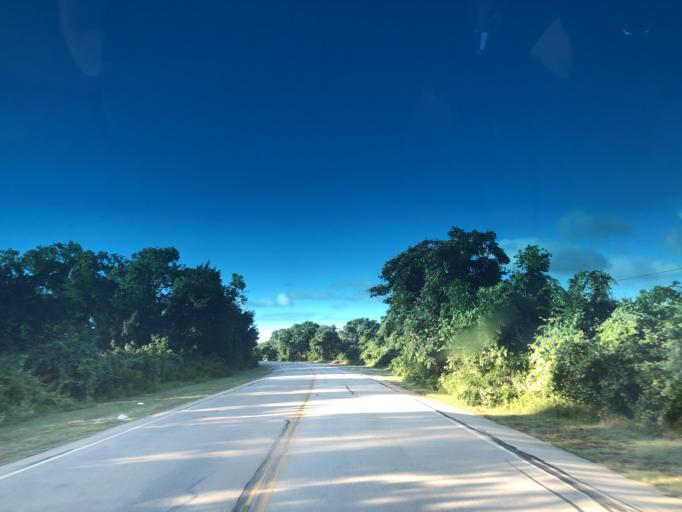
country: US
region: Texas
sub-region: Dallas County
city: Grand Prairie
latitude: 32.7826
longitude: -97.0169
